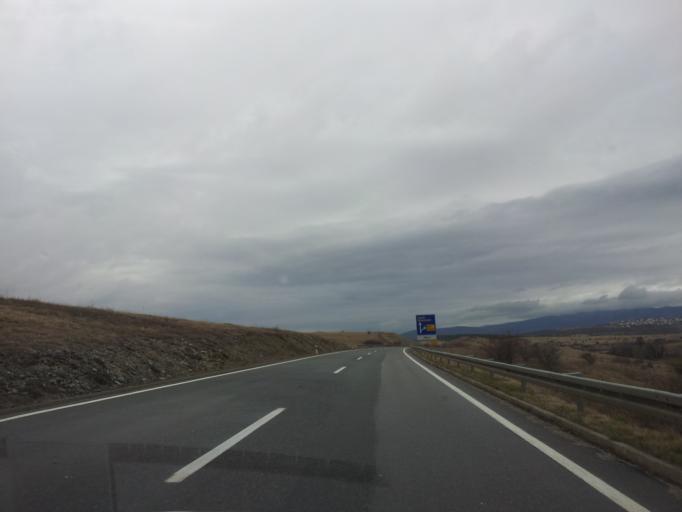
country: HR
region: Zadarska
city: Gracac
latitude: 44.4983
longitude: 15.7466
